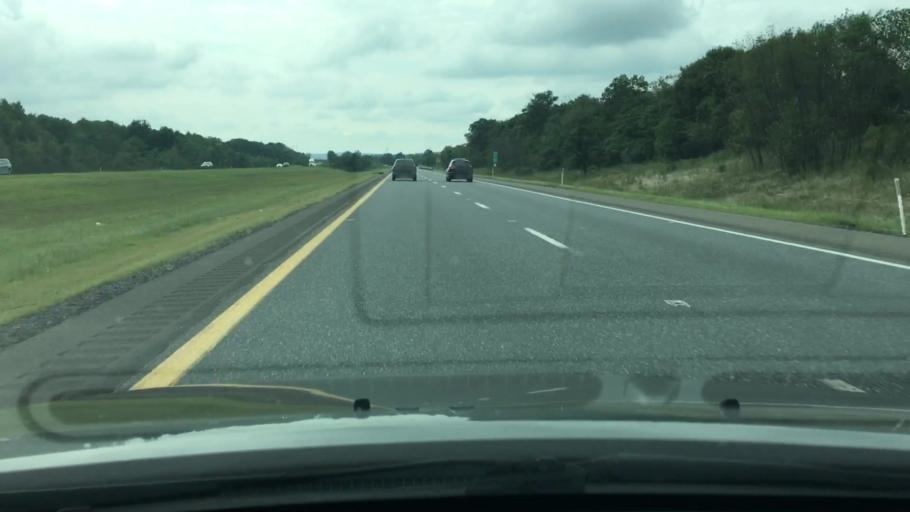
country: US
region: Pennsylvania
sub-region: Schuylkill County
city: Tremont
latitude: 40.6486
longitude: -76.4168
